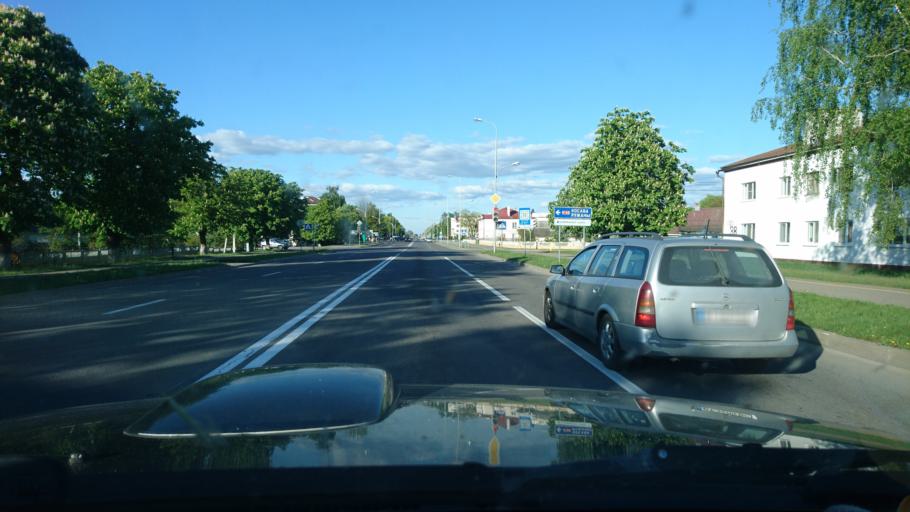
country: BY
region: Brest
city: Ivatsevichy
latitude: 52.7075
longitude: 25.3343
